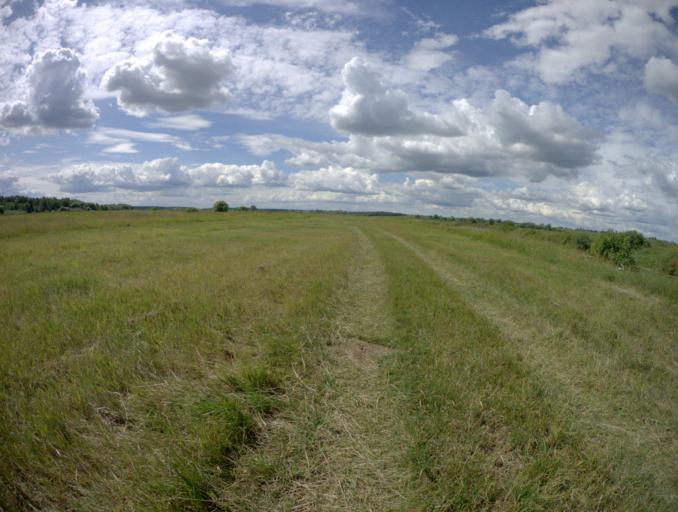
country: RU
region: Vladimir
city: Orgtrud
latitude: 56.3050
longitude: 40.6520
